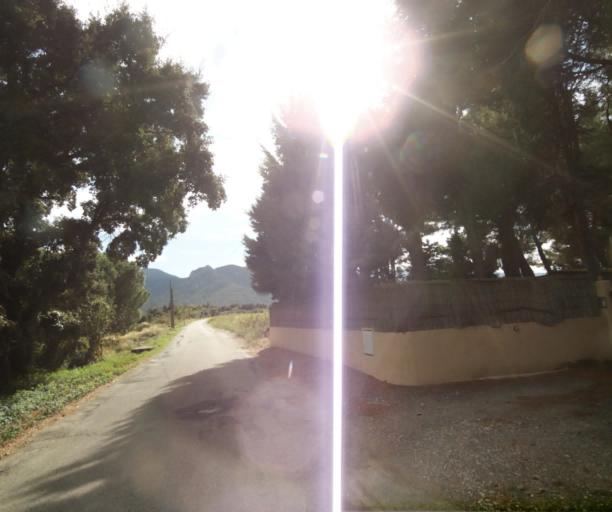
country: FR
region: Languedoc-Roussillon
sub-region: Departement des Pyrenees-Orientales
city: Sant Andreu de Sureda
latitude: 42.5425
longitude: 2.9893
